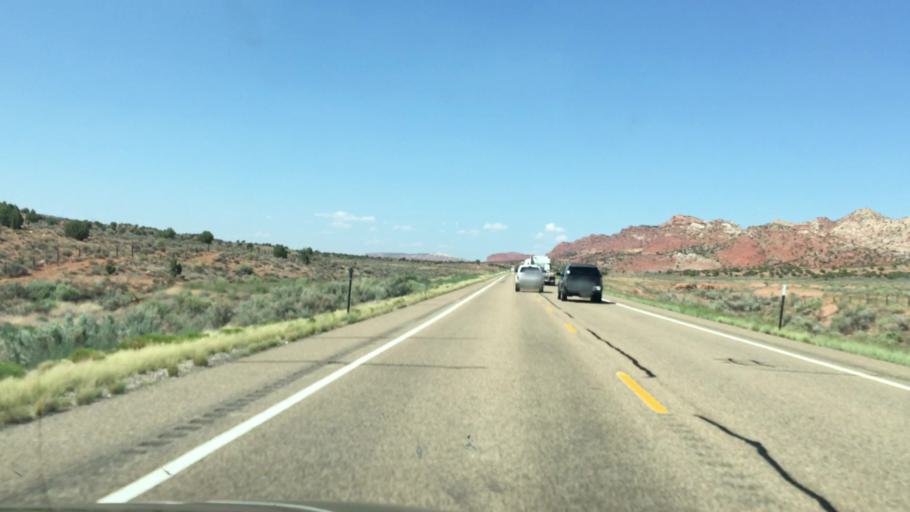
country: US
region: Utah
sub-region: Kane County
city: Kanab
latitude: 37.1393
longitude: -111.9748
